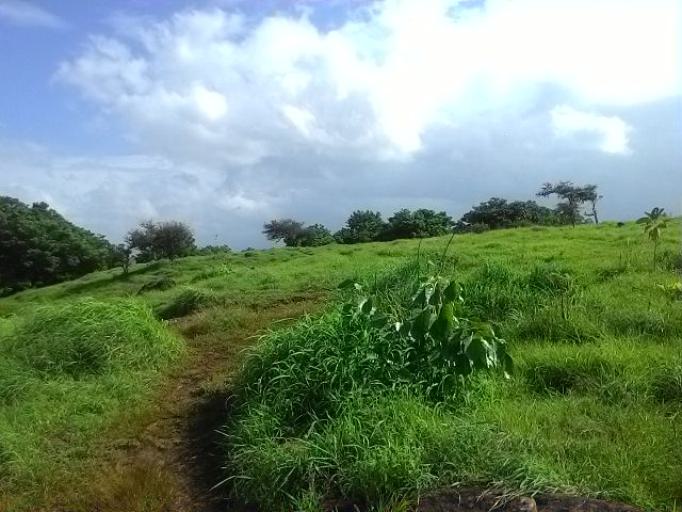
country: IN
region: Maharashtra
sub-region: Pune Division
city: Khadki
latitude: 18.5488
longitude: 73.7804
